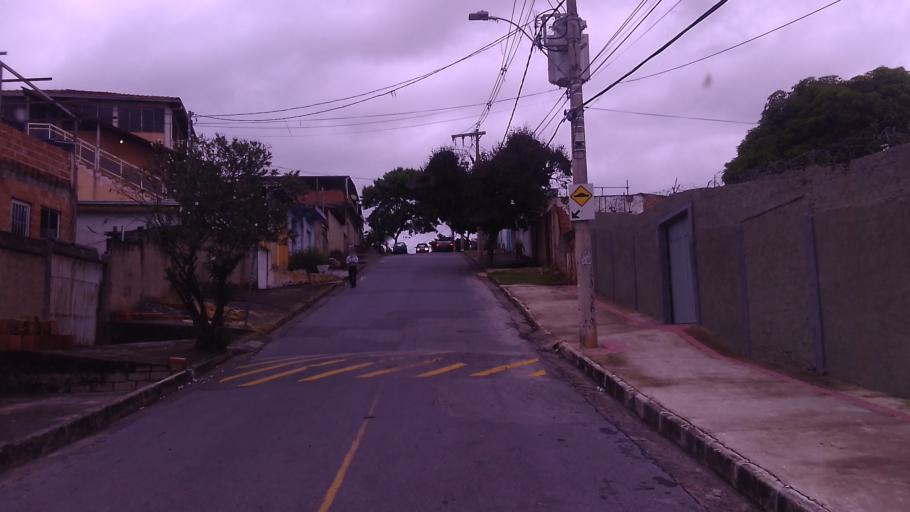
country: BR
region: Minas Gerais
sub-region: Santa Luzia
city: Santa Luzia
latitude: -19.8352
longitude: -43.9056
